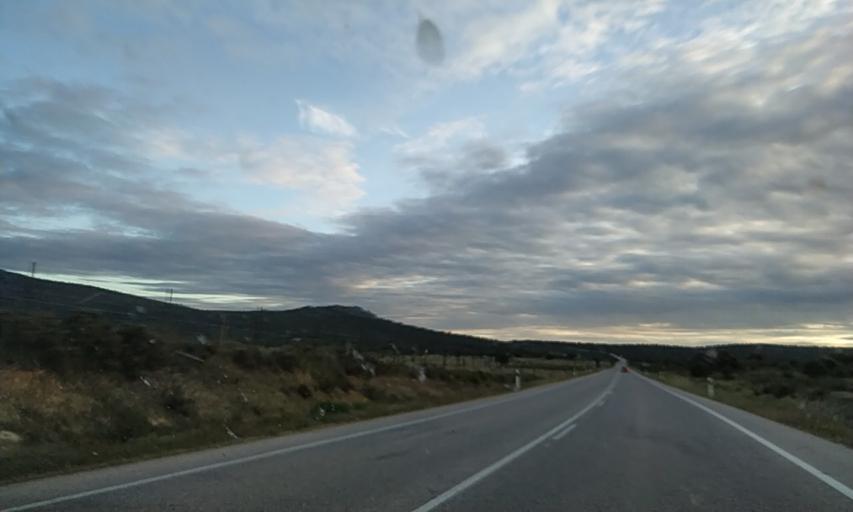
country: ES
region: Extremadura
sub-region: Provincia de Caceres
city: Malpartida de Caceres
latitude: 39.3194
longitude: -6.5020
